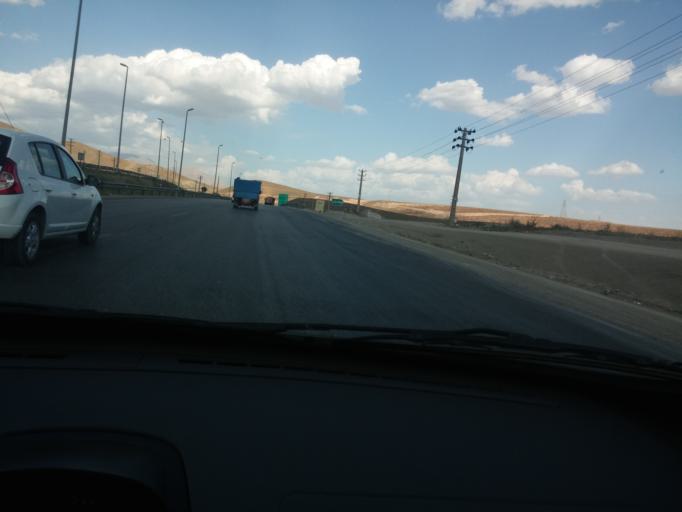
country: IR
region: Tehran
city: Damavand
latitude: 35.7076
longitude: 51.9791
